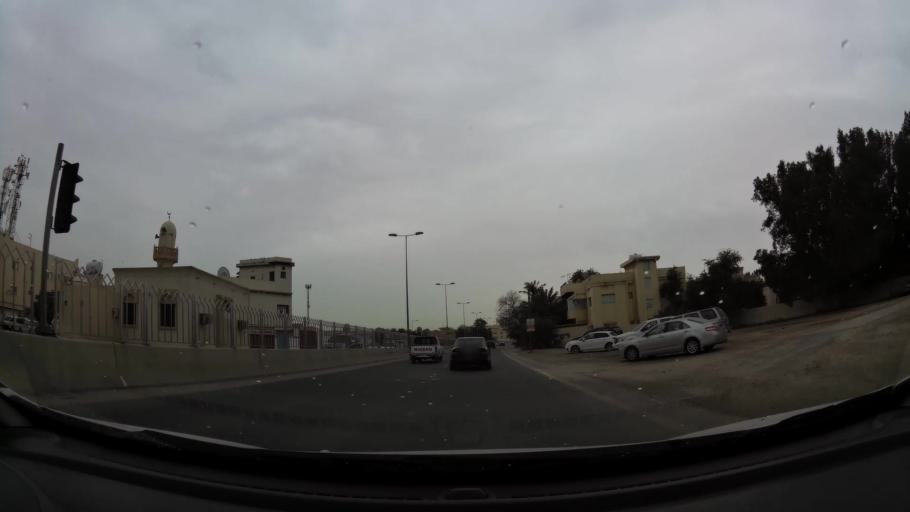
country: BH
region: Manama
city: Jidd Hafs
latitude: 26.2140
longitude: 50.5340
